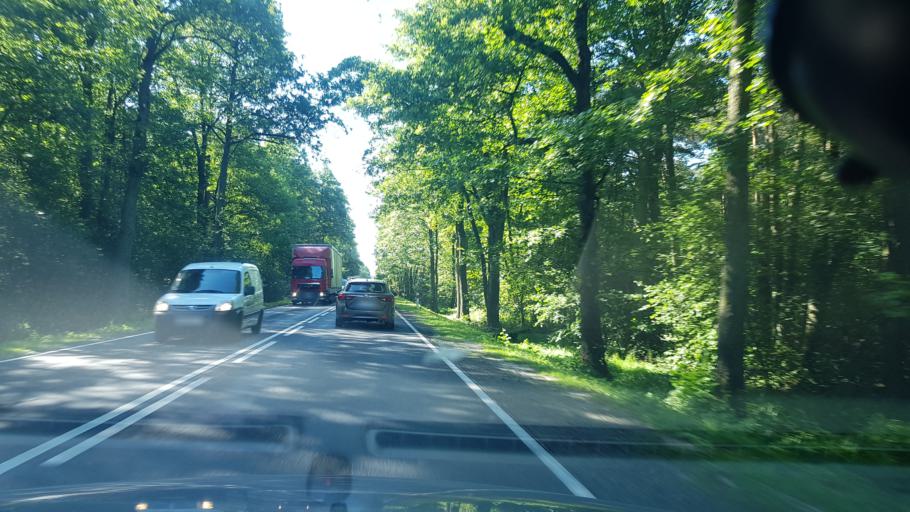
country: PL
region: Masovian Voivodeship
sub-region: Powiat wyszkowski
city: Branszczyk
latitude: 52.5792
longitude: 21.5345
